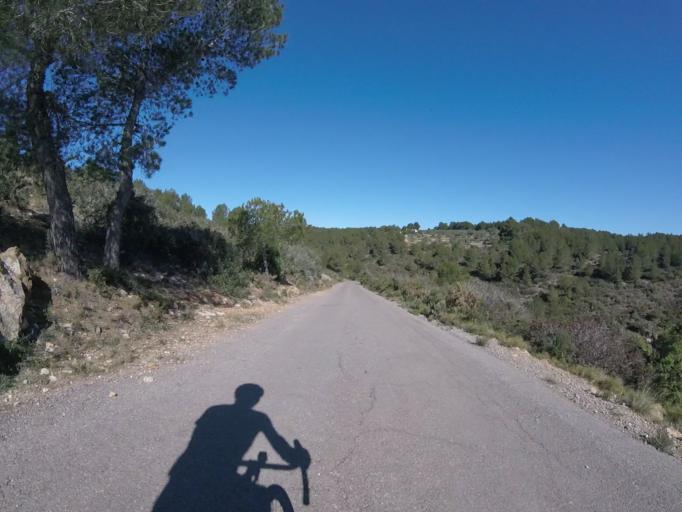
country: ES
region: Valencia
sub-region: Provincia de Castello
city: Benicassim
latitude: 40.0797
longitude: 0.0898
